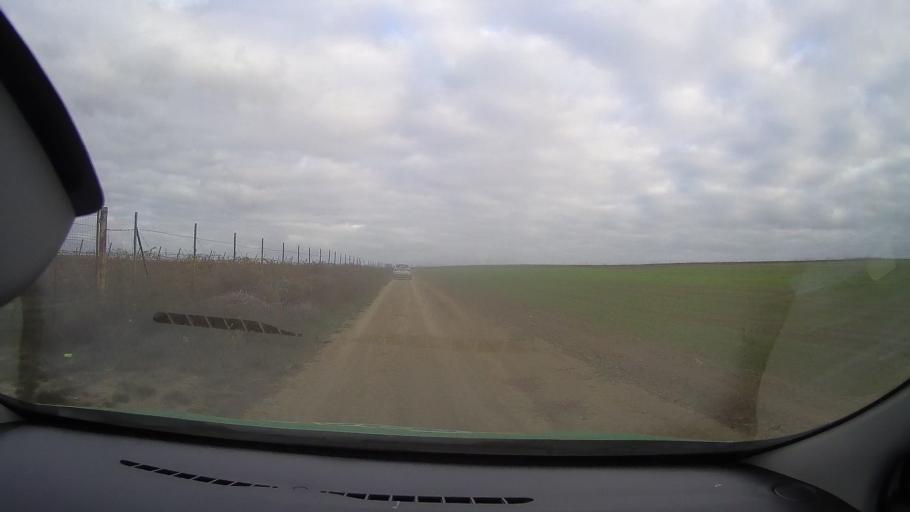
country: RO
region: Tulcea
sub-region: Comuna Jurilovca
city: Jurilovca
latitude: 44.7679
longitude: 28.9068
